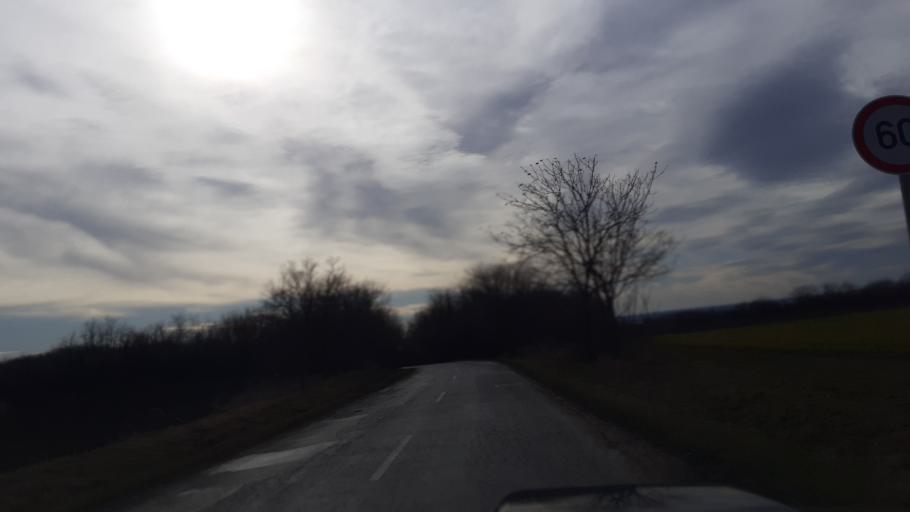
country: HU
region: Fejer
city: Sarbogard
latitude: 46.9131
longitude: 18.6665
